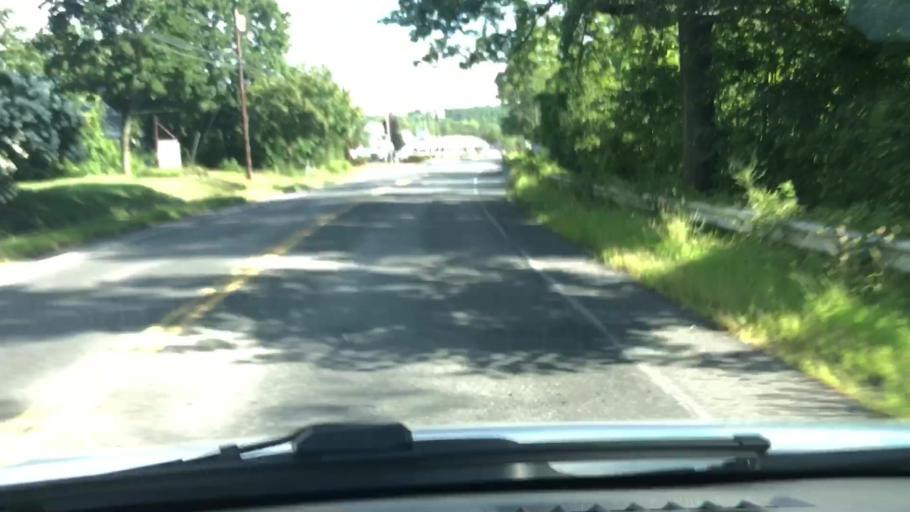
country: US
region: Massachusetts
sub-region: Franklin County
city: Turners Falls
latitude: 42.5996
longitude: -72.5641
